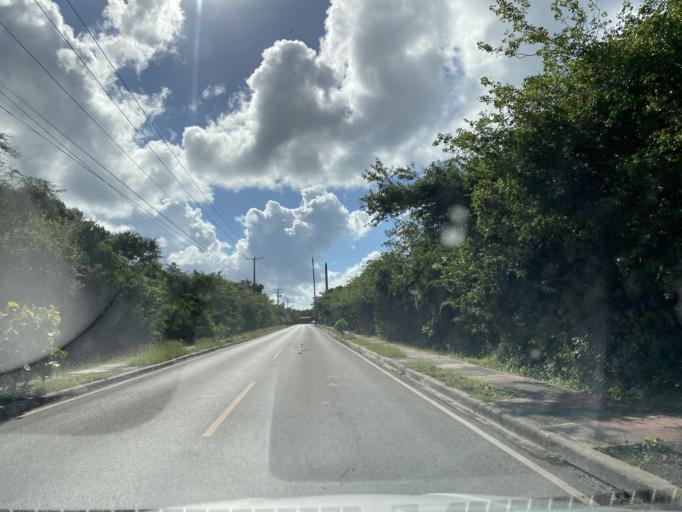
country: DO
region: La Altagracia
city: San Rafael del Yuma
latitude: 18.3355
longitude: -68.8094
